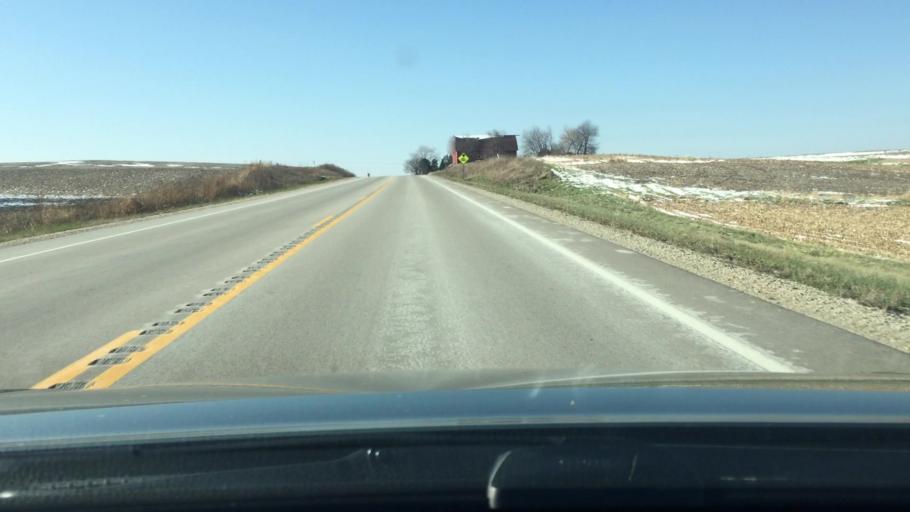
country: US
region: Wisconsin
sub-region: Jefferson County
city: Lake Mills
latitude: 43.0075
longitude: -88.8896
